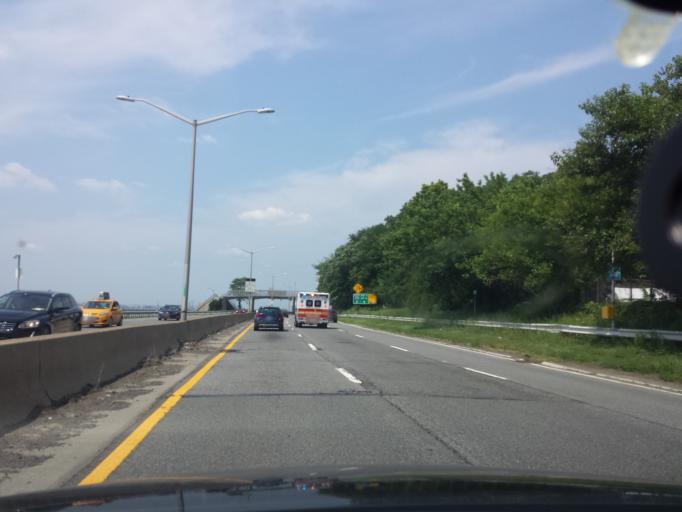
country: US
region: New York
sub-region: Kings County
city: Bensonhurst
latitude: 40.6283
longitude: -74.0411
